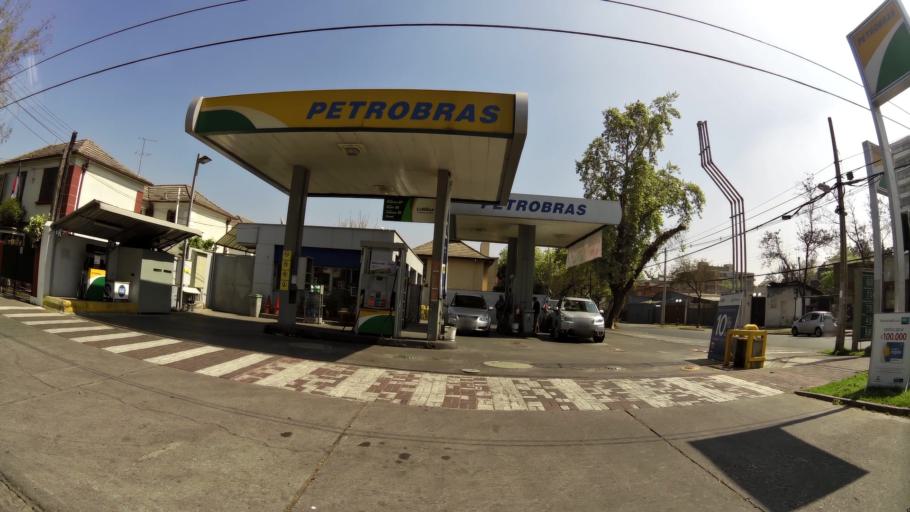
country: CL
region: Santiago Metropolitan
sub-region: Provincia de Santiago
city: Villa Presidente Frei, Nunoa, Santiago, Chile
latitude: -33.4452
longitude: -70.6029
